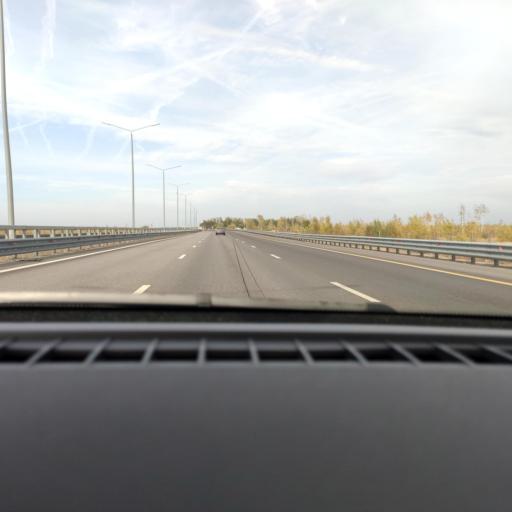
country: RU
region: Voronezj
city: Somovo
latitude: 51.7553
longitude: 39.3067
